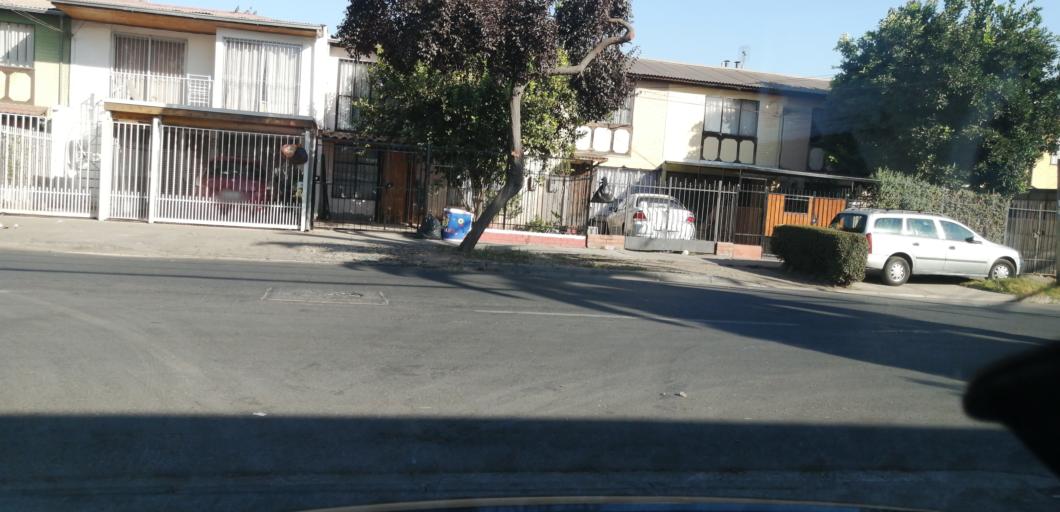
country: CL
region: Santiago Metropolitan
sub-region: Provincia de Santiago
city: Lo Prado
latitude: -33.4608
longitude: -70.7462
